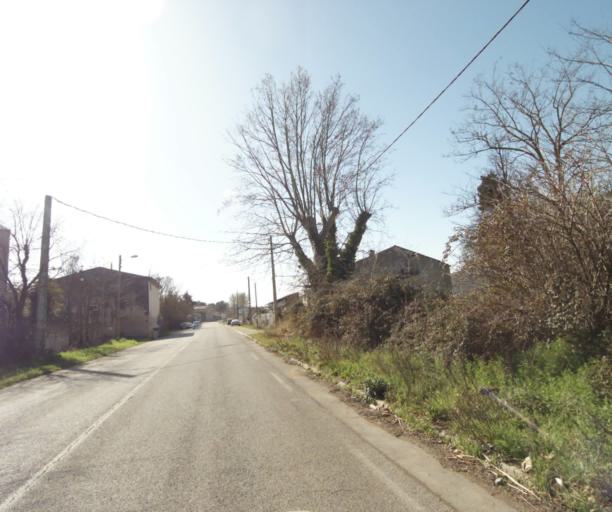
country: FR
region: Provence-Alpes-Cote d'Azur
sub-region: Departement des Bouches-du-Rhone
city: Cabries
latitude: 43.4214
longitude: 5.3834
